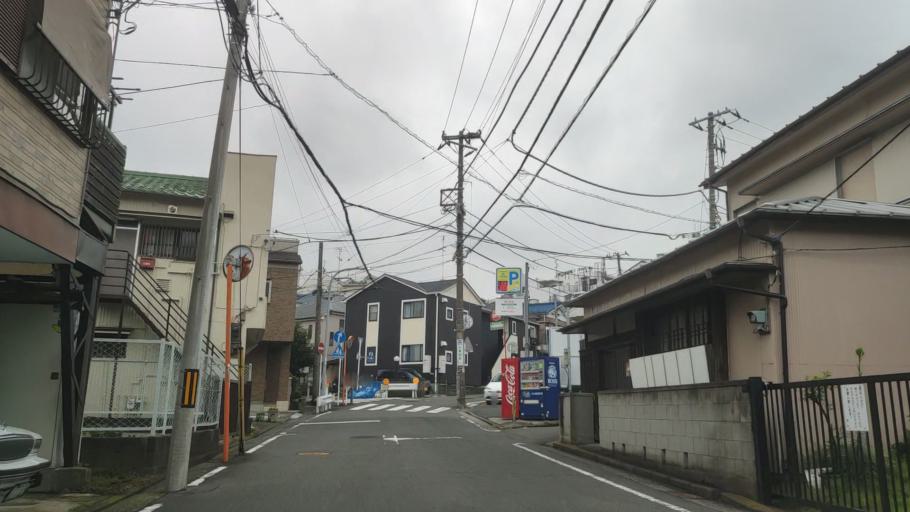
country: JP
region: Kanagawa
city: Yokohama
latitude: 35.4453
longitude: 139.6053
